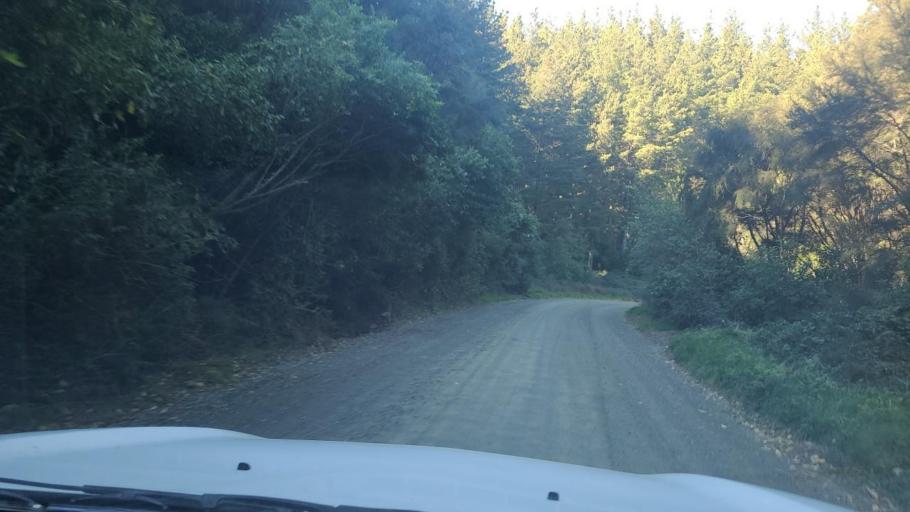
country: NZ
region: Hawke's Bay
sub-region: Napier City
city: Taradale
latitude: -39.4157
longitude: 176.4876
